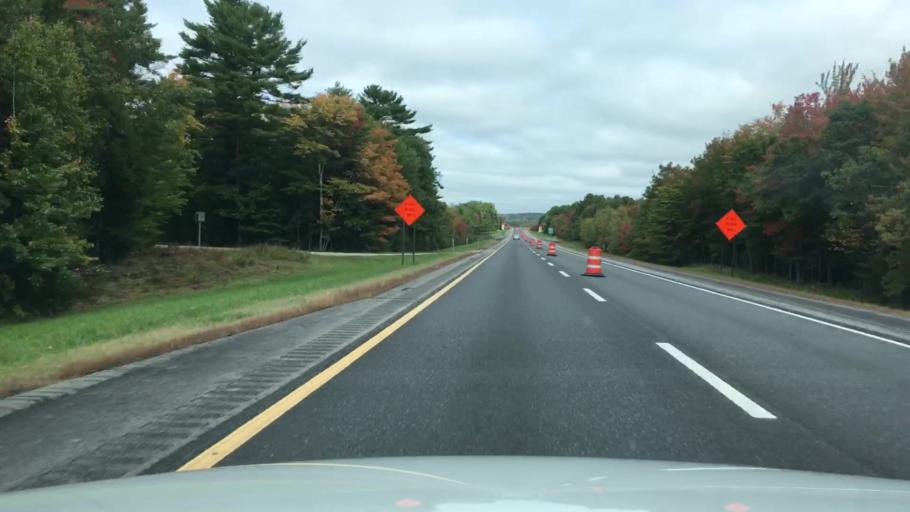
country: US
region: Maine
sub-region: Sagadahoc County
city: Richmond
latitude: 44.1350
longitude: -69.8445
